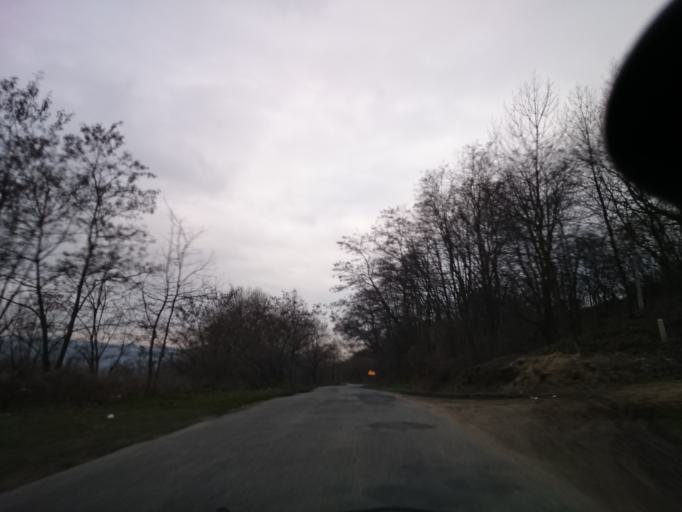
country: PL
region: Lower Silesian Voivodeship
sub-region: Powiat zabkowicki
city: Zabkowice Slaskie
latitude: 50.5285
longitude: 16.8172
